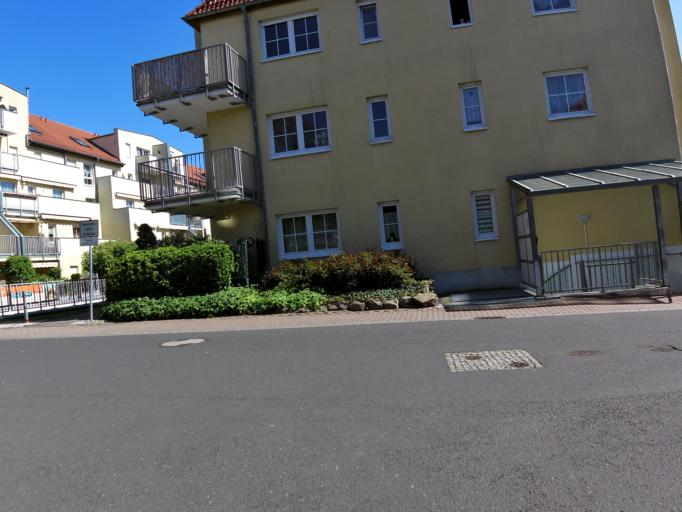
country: DE
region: Saxony
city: Leipzig
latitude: 51.3660
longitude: 12.3451
